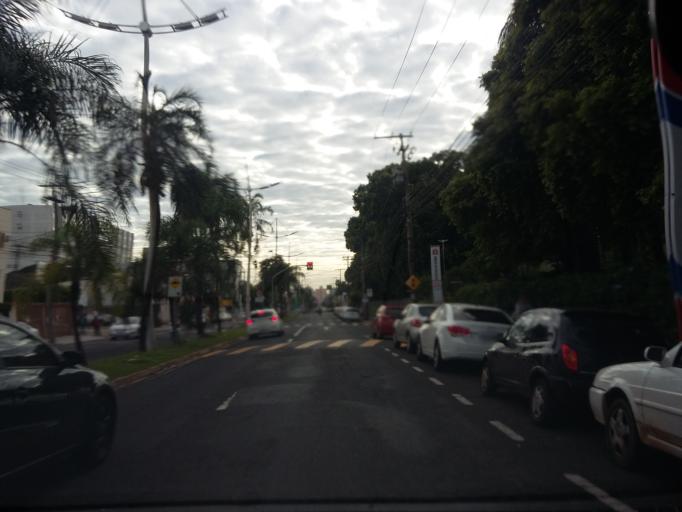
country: BR
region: Sao Paulo
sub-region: Sao Jose Do Rio Preto
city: Sao Jose do Rio Preto
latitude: -20.8308
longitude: -49.3981
